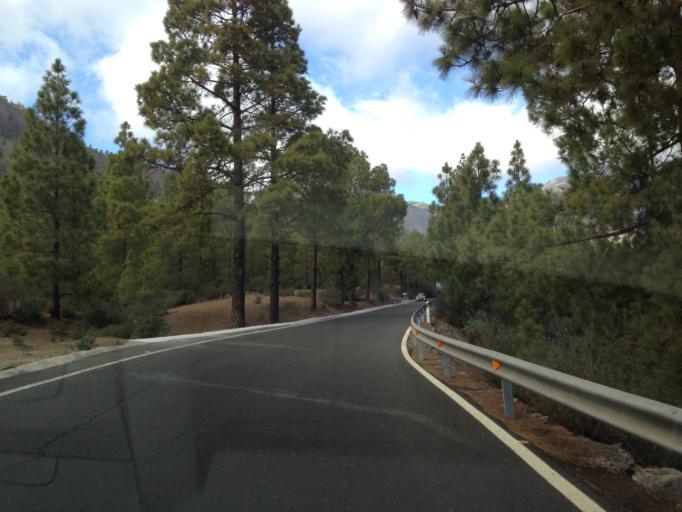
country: ES
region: Canary Islands
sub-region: Provincia de Las Palmas
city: San Bartolome
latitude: 27.9141
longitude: -15.5740
